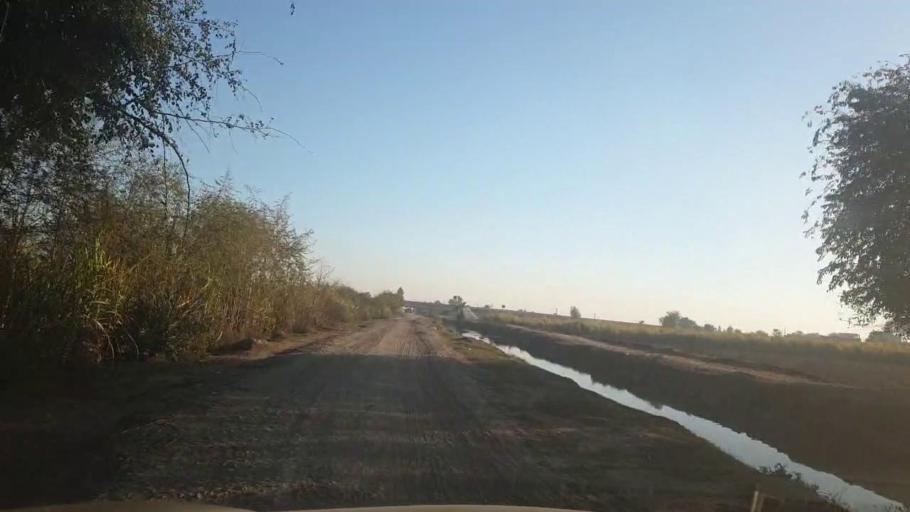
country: PK
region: Sindh
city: Ghotki
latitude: 28.0114
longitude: 69.2687
